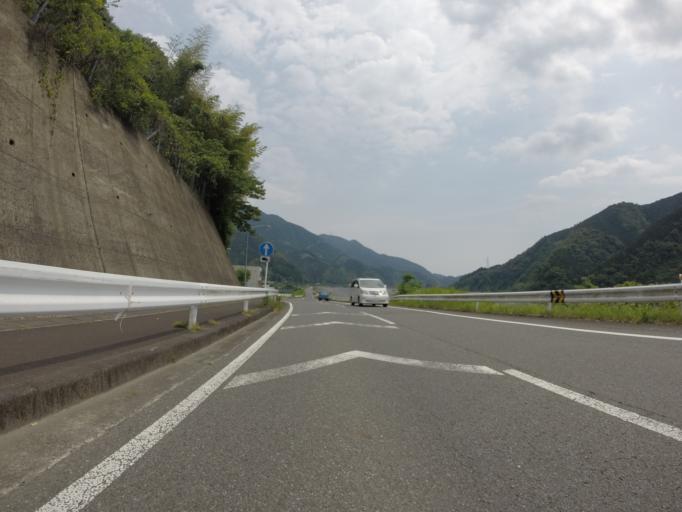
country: JP
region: Shizuoka
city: Shizuoka-shi
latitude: 35.1022
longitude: 138.3673
